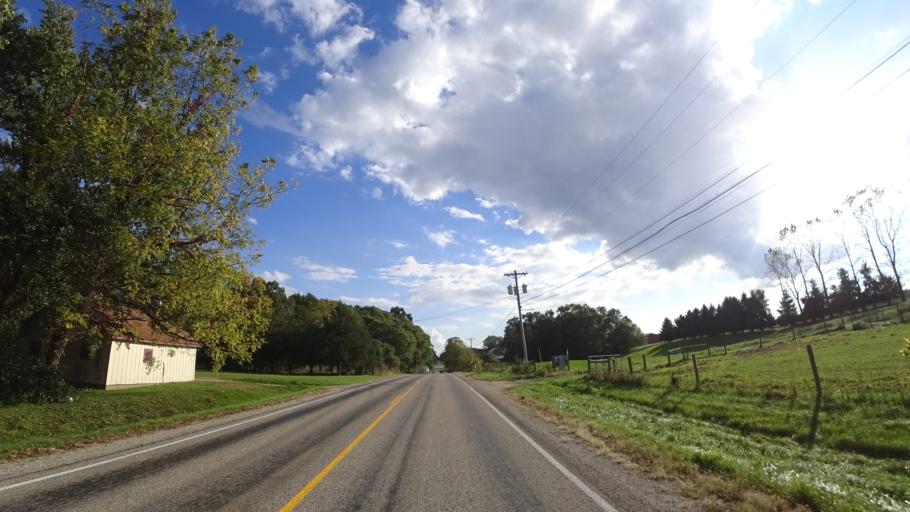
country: US
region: Michigan
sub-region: Saint Joseph County
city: Sturgis
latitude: 41.8483
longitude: -85.4287
